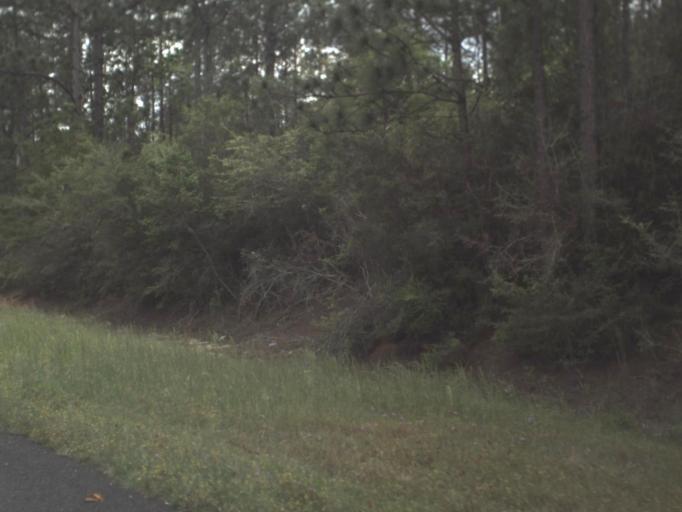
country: US
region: Florida
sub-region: Escambia County
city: Molino
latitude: 30.8130
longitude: -87.3354
